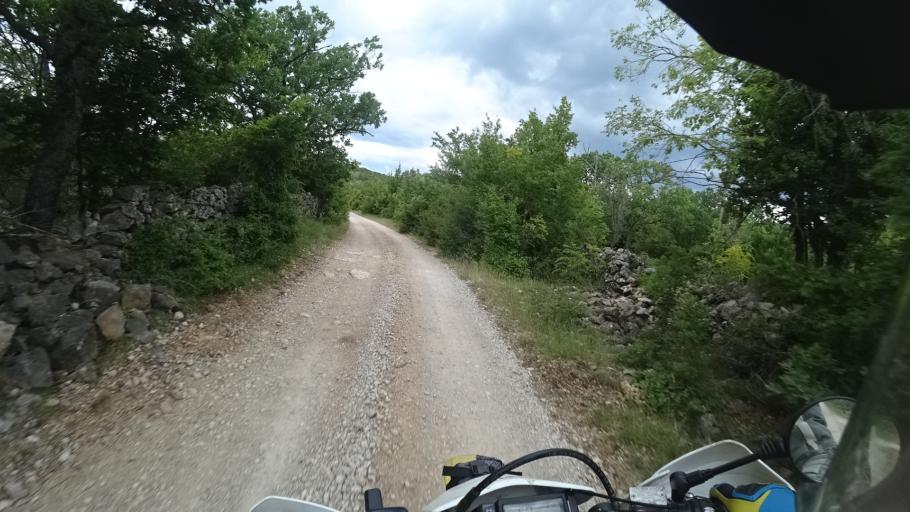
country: HR
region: Sibensko-Kniniska
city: Kistanje
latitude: 44.0982
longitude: 16.0188
